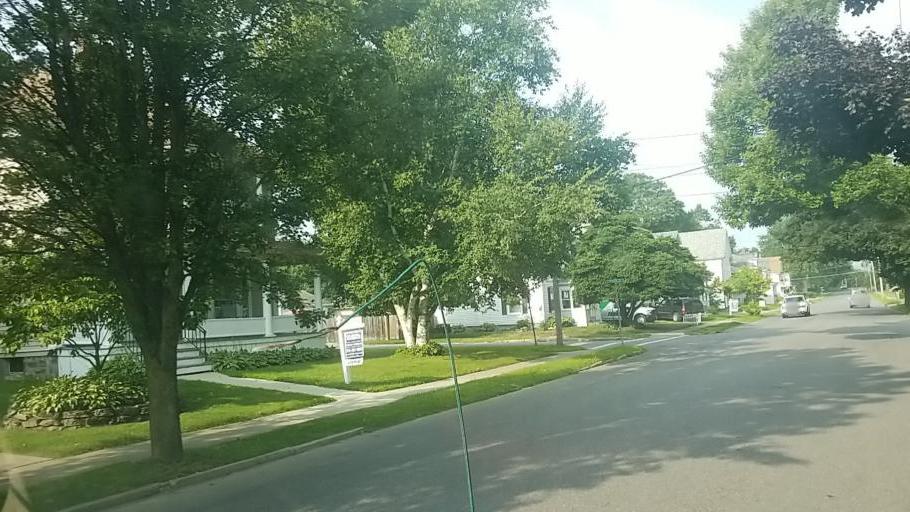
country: US
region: New York
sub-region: Fulton County
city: Gloversville
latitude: 43.0511
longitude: -74.3295
